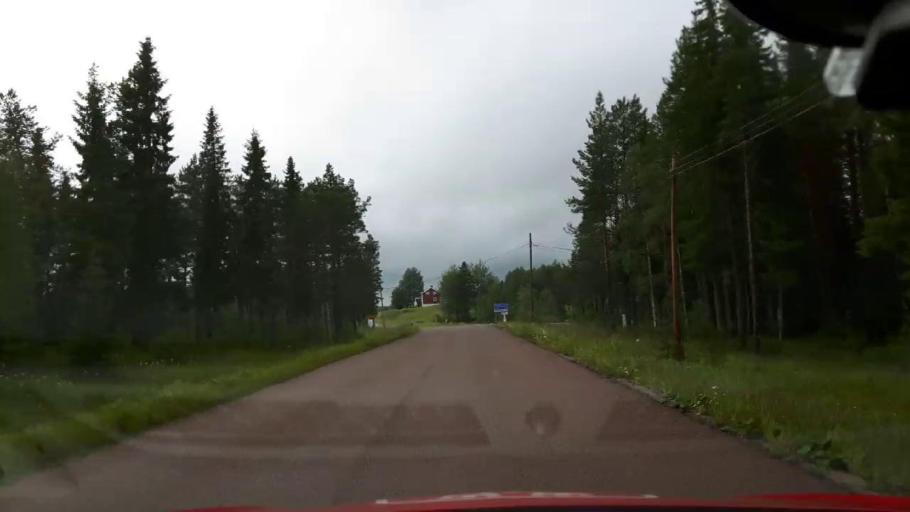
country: SE
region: Jaemtland
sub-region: Krokoms Kommun
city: Valla
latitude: 63.3872
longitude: 13.8217
